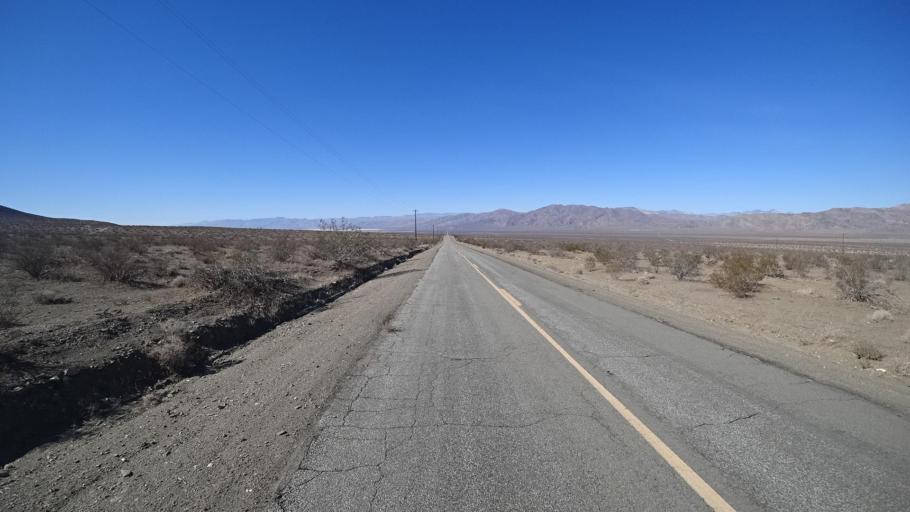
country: US
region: California
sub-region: Kern County
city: Ridgecrest
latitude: 35.3806
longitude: -117.6793
